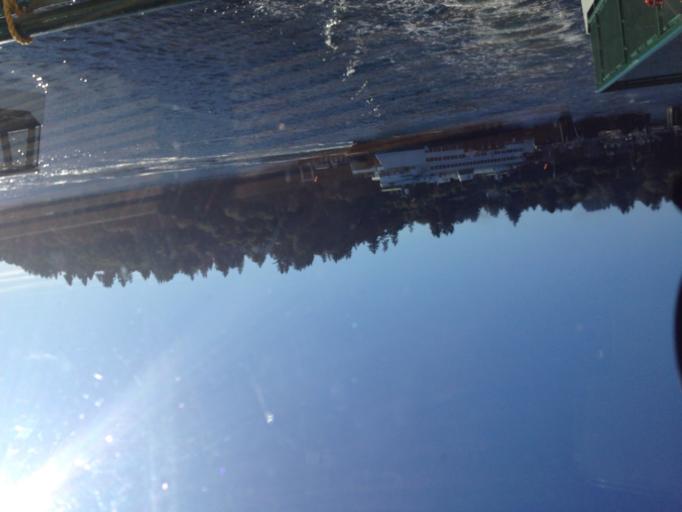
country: US
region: Washington
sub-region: Kitsap County
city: Southworth
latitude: 47.5129
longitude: -122.4622
